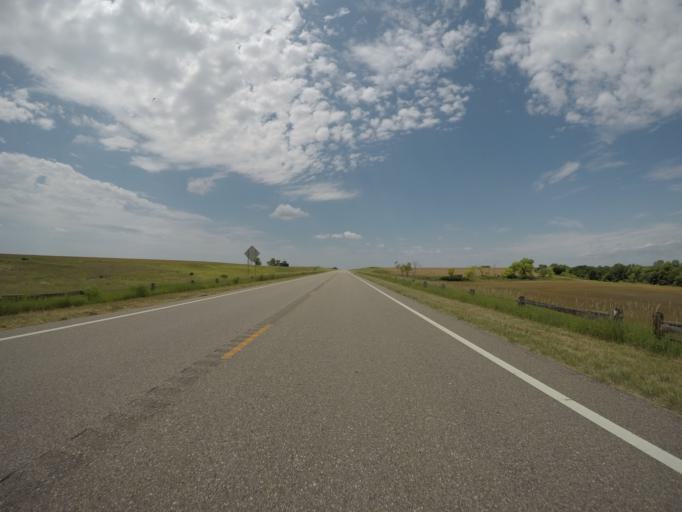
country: US
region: Kansas
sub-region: Graham County
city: Hill City
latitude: 39.3905
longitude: -99.6502
